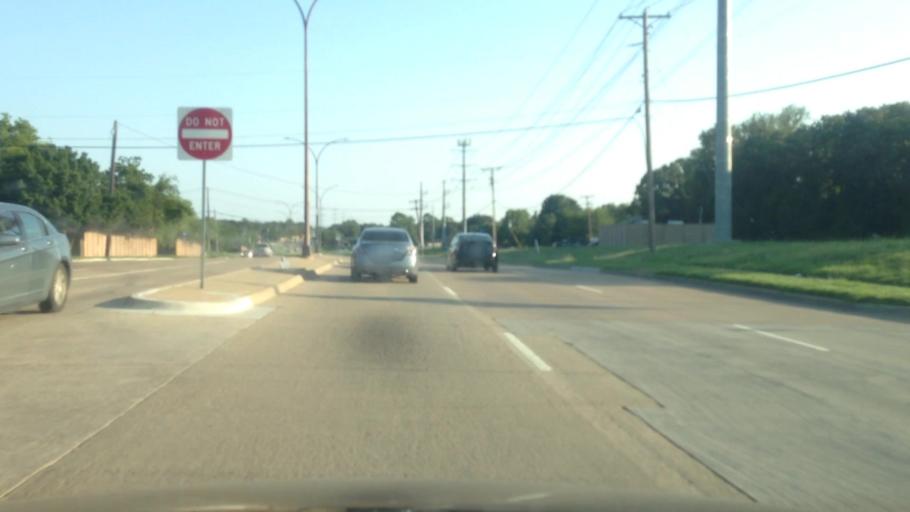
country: US
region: Texas
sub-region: Tarrant County
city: Pantego
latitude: 32.7060
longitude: -97.1909
